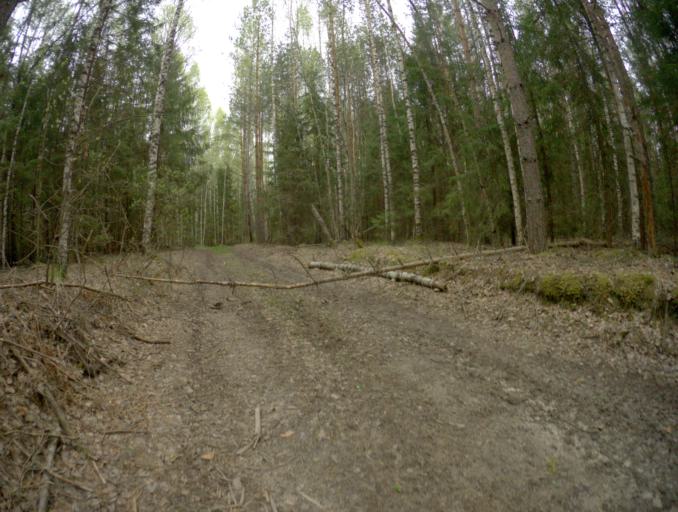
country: RU
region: Vladimir
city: Golovino
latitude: 55.8876
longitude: 40.4019
